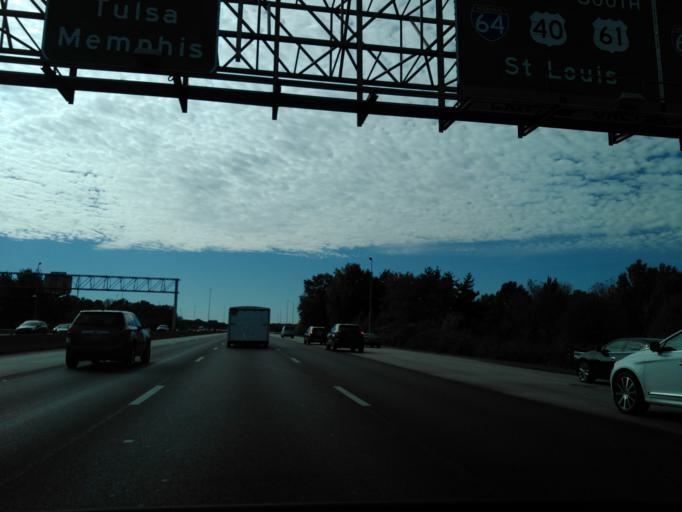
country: US
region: Missouri
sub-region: Saint Louis County
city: Creve Coeur
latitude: 38.6467
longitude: -90.4490
